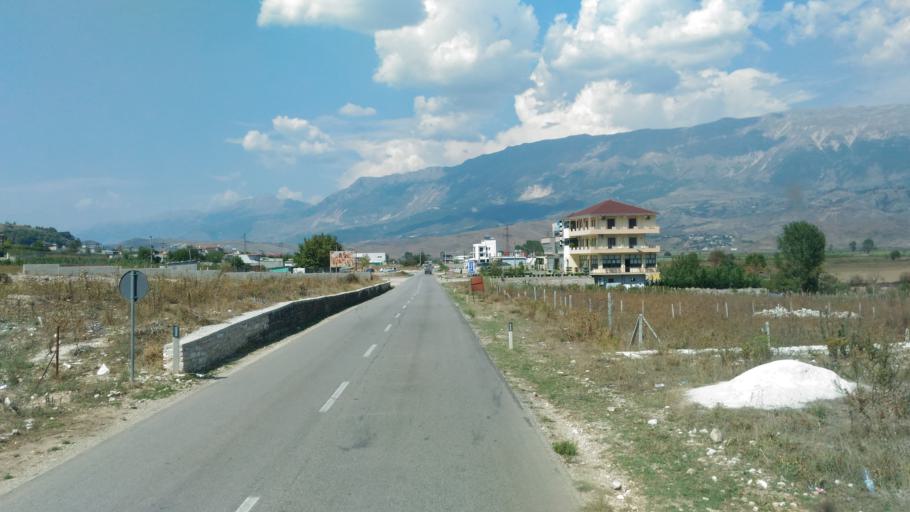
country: AL
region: Gjirokaster
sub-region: Rrethi i Gjirokastres
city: Dervician
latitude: 40.0469
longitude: 20.1767
